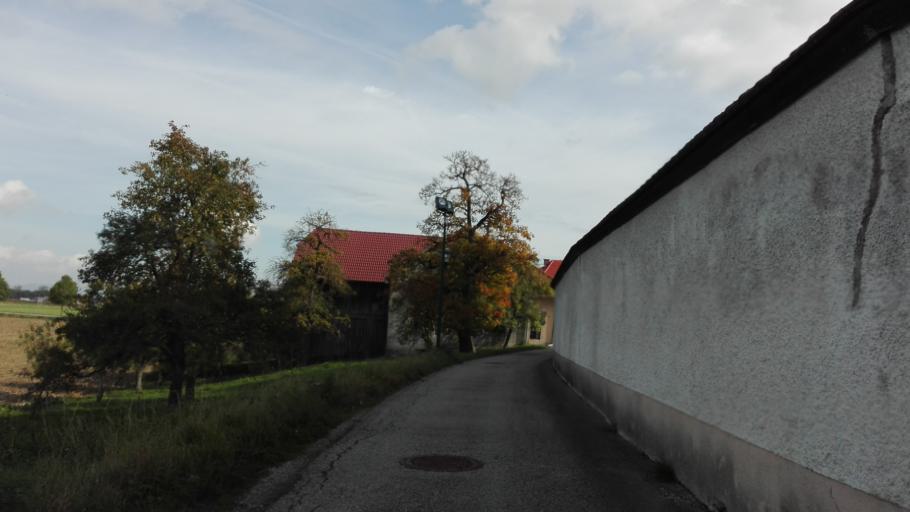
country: AT
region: Upper Austria
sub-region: Wels-Land
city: Marchtrenk
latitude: 48.1643
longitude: 14.1273
